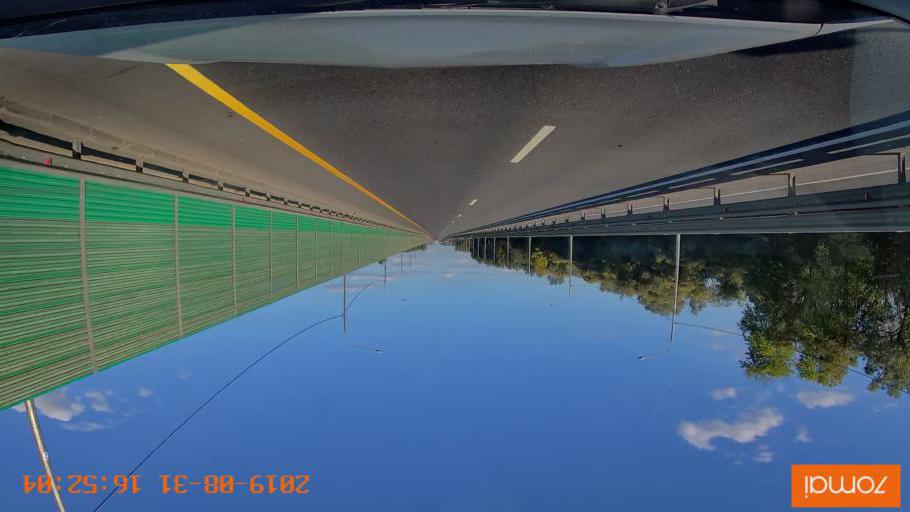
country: RU
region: Kaluga
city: Pyatovskiy
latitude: 54.7360
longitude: 36.1840
